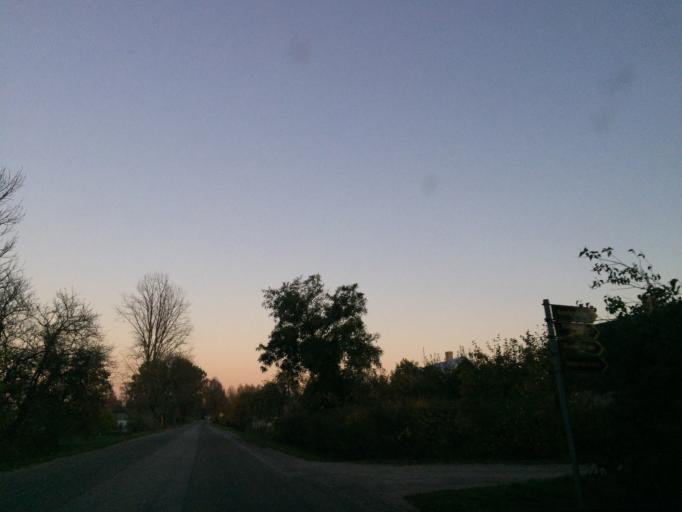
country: LT
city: Vieksniai
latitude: 56.3837
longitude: 22.6198
